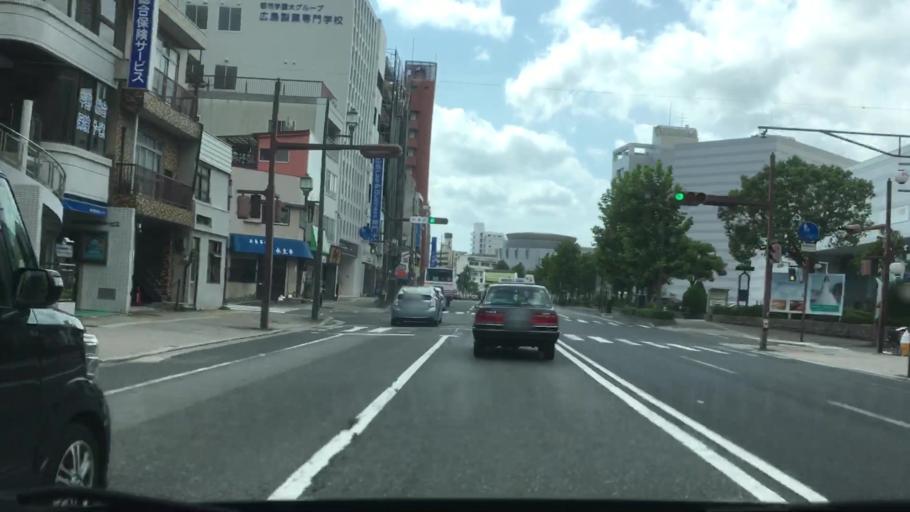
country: JP
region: Hiroshima
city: Hiroshima-shi
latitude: 34.3895
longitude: 132.4501
